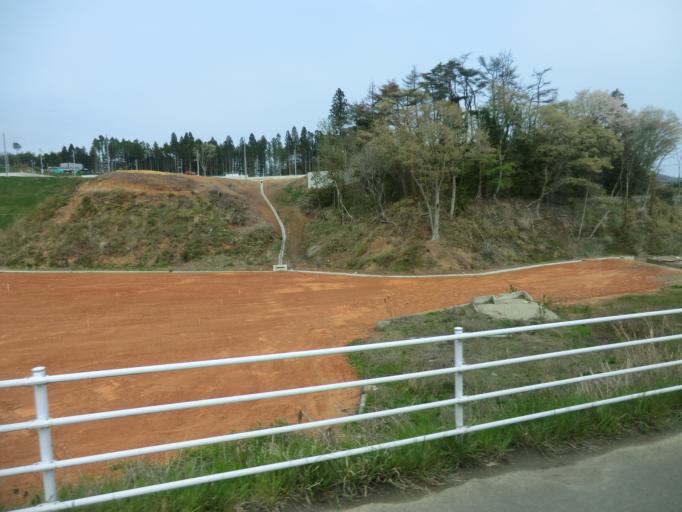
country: JP
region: Iwate
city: Ofunato
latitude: 38.8761
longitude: 141.5805
